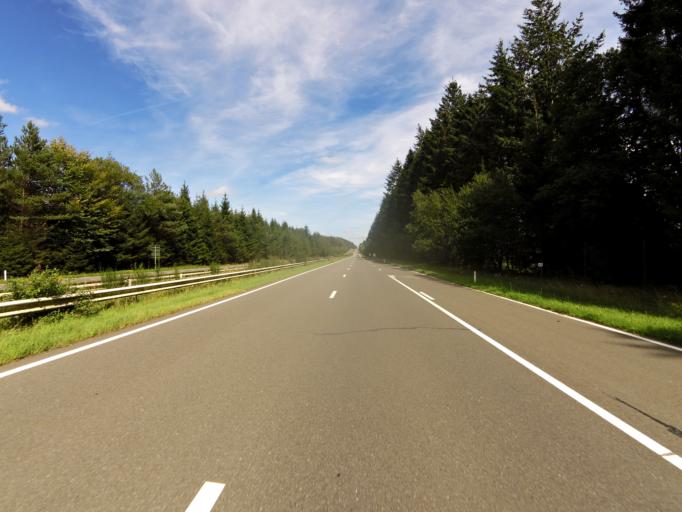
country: BE
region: Wallonia
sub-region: Province du Luxembourg
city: Saint-Hubert
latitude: 50.0521
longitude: 5.4002
